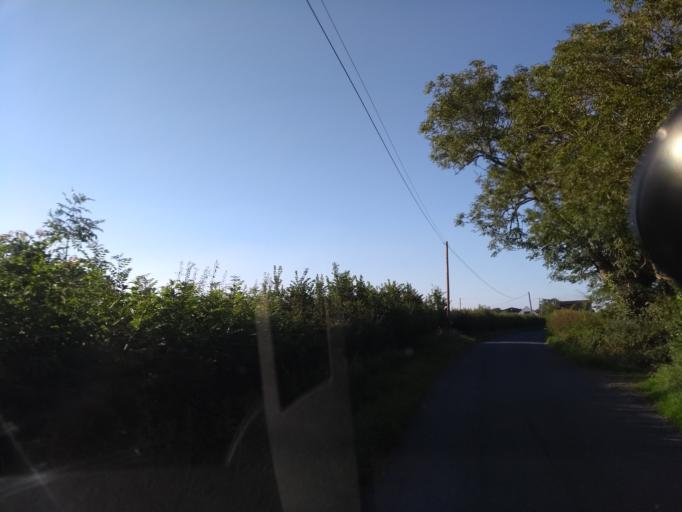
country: GB
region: England
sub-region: Somerset
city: Axbridge
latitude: 51.2645
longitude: -2.8672
